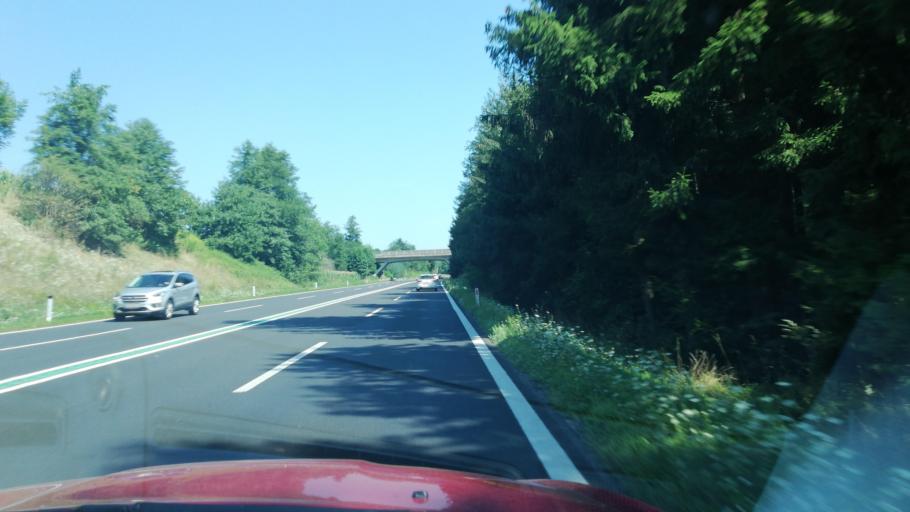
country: AT
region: Carinthia
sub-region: Politischer Bezirk Sankt Veit an der Glan
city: Sankt Veit an der Glan
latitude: 46.7722
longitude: 14.3807
